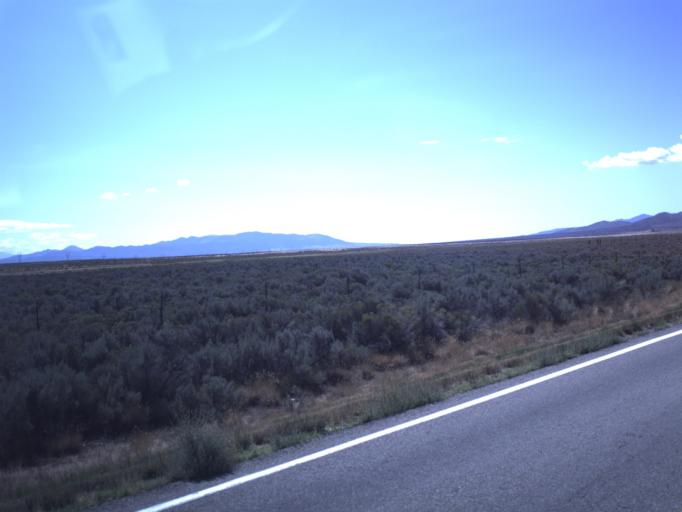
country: US
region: Utah
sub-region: Tooele County
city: Tooele
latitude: 40.2329
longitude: -112.4029
